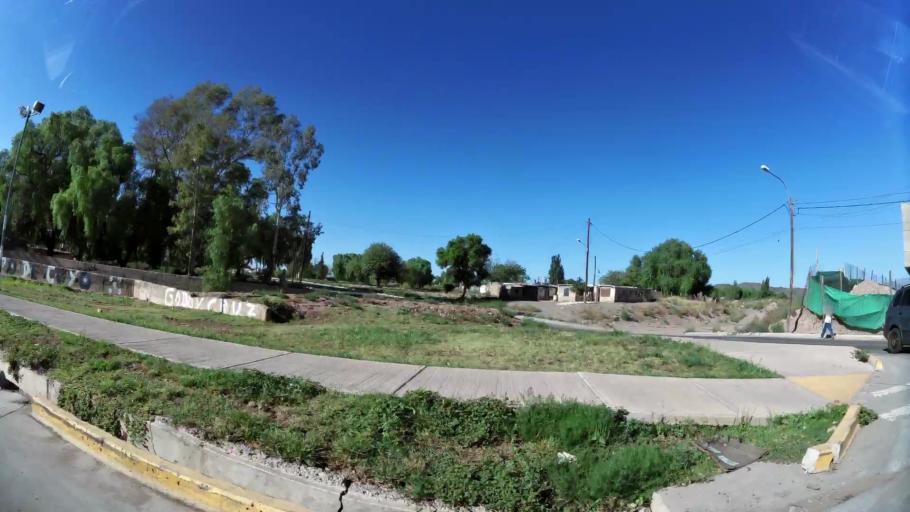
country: AR
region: Mendoza
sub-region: Departamento de Godoy Cruz
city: Godoy Cruz
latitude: -32.9253
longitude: -68.8688
